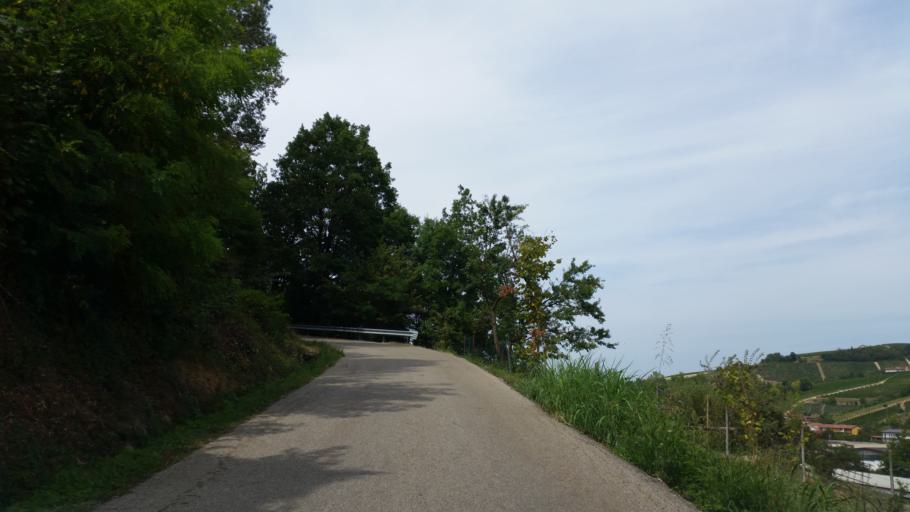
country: IT
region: Piedmont
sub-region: Provincia di Cuneo
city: Ricca
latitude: 44.6627
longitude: 8.0414
